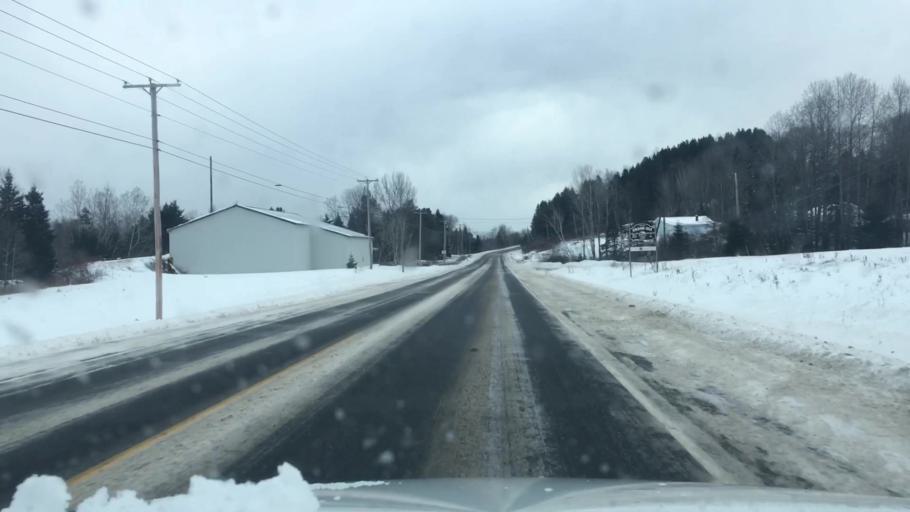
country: US
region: Maine
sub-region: Aroostook County
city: Madawaska
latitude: 47.3269
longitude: -68.1802
